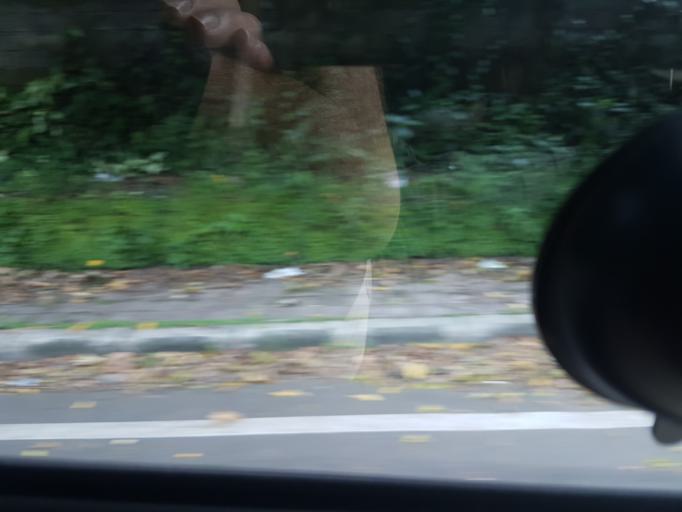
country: ID
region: Bali
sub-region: Kabupaten Gianyar
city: Ubud
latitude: -8.5160
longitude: 115.2935
